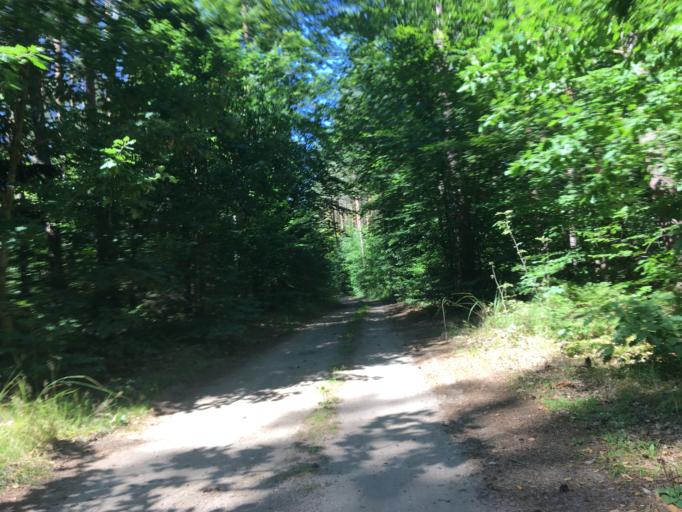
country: DE
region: Brandenburg
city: Rheinsberg
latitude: 53.1294
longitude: 12.9669
